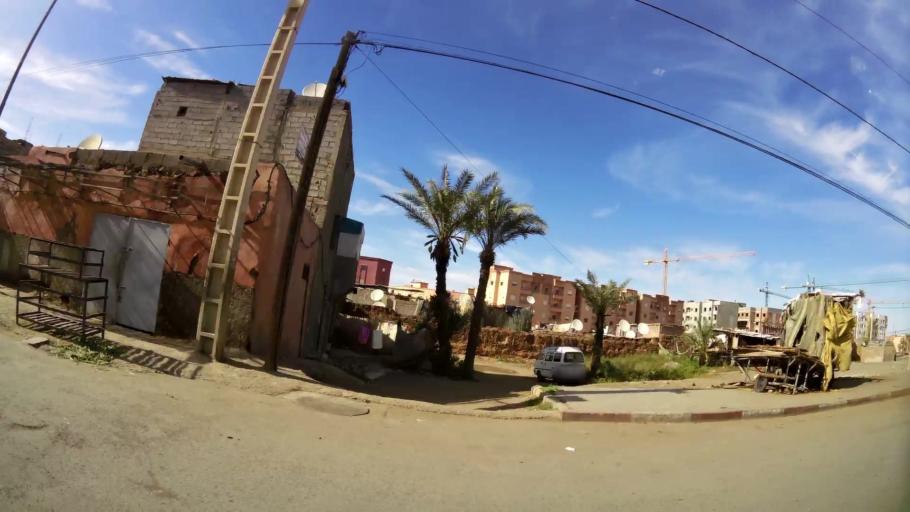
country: MA
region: Marrakech-Tensift-Al Haouz
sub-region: Marrakech
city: Marrakesh
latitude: 31.6529
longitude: -8.0298
